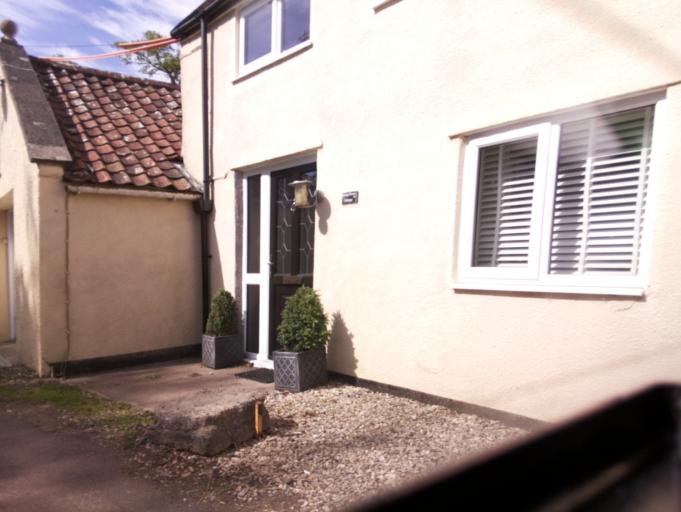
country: GB
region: England
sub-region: South Gloucestershire
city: Horton
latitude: 51.5332
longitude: -2.3626
